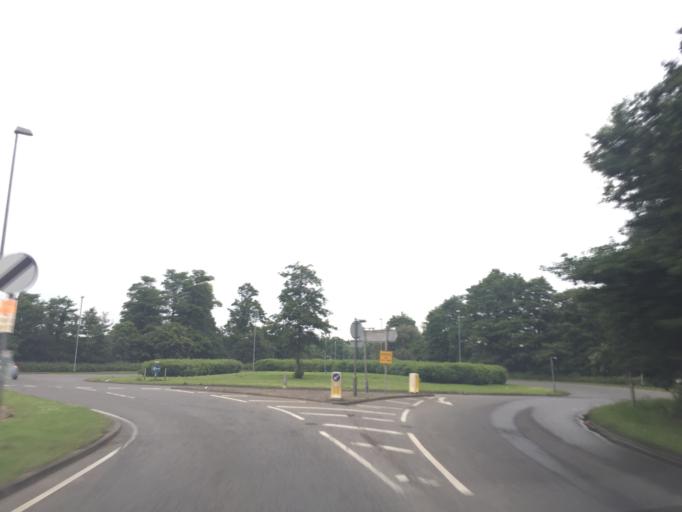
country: GB
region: England
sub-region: Greater London
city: Collier Row
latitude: 51.6544
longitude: 0.1717
